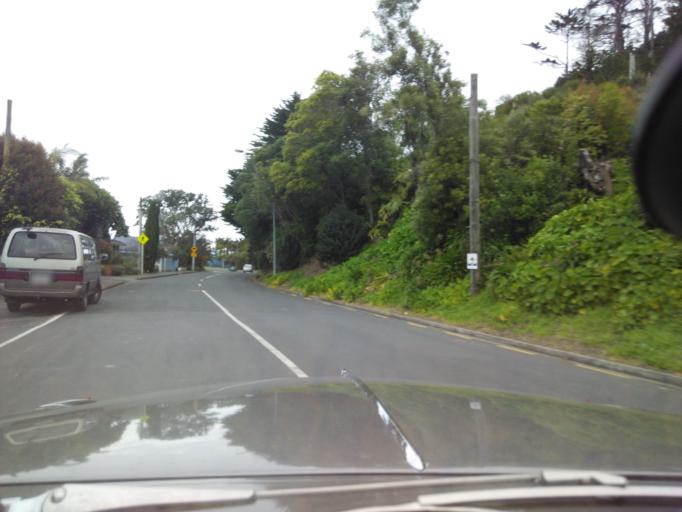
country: NZ
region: Auckland
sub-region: Auckland
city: Warkworth
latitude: -36.5435
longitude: 174.7040
